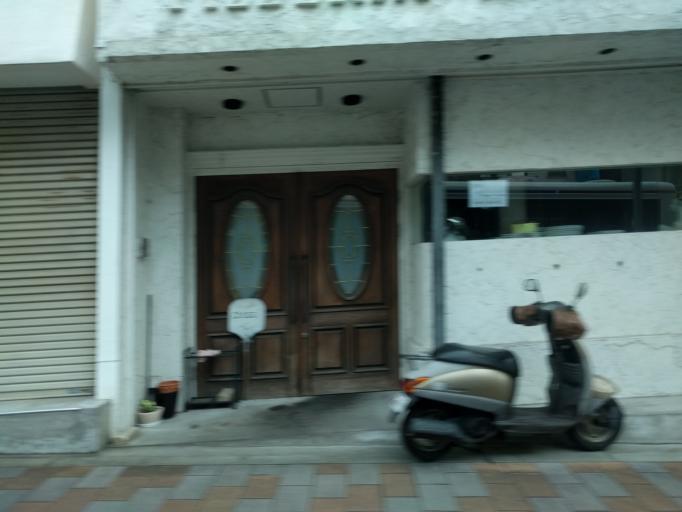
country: JP
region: Kanagawa
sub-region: Kawasaki-shi
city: Kawasaki
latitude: 35.5940
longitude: 139.6707
